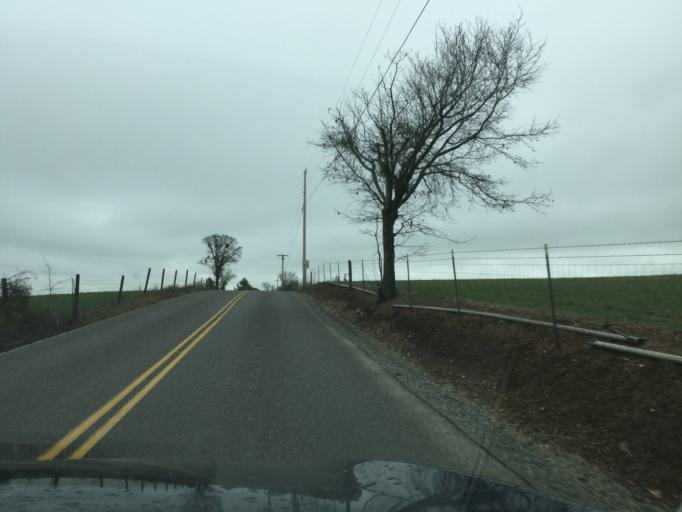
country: US
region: Oregon
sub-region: Jackson County
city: Central Point
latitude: 42.3902
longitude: -122.9677
